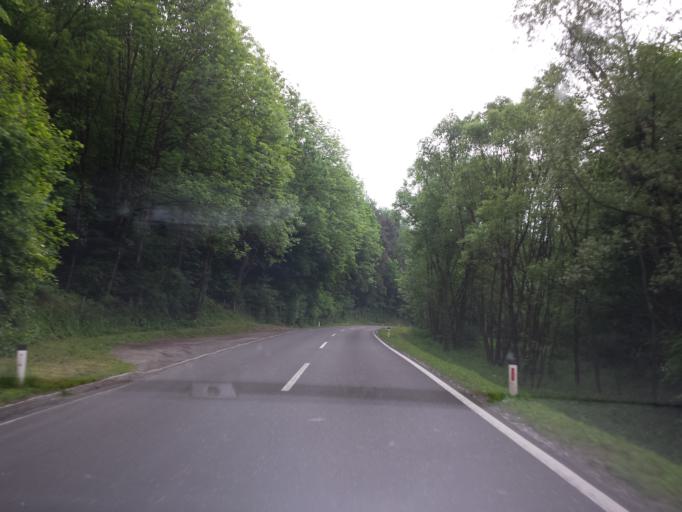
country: AT
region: Styria
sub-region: Politischer Bezirk Weiz
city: Floing
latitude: 47.2544
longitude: 15.7233
